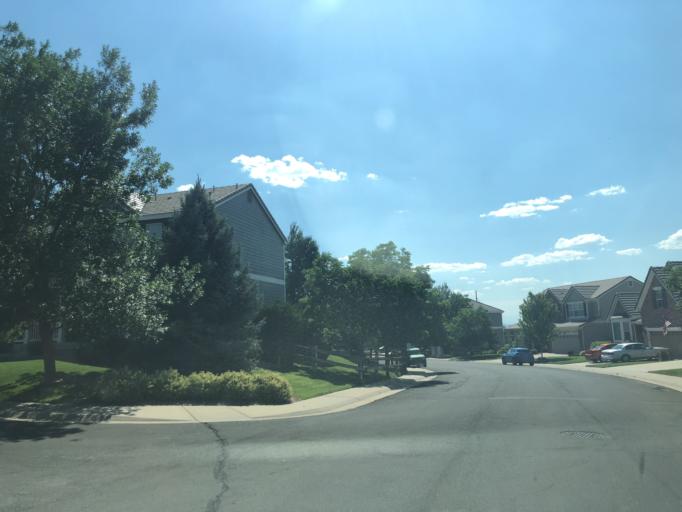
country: US
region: Colorado
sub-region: Arapahoe County
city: Dove Valley
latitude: 39.6091
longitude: -104.7887
